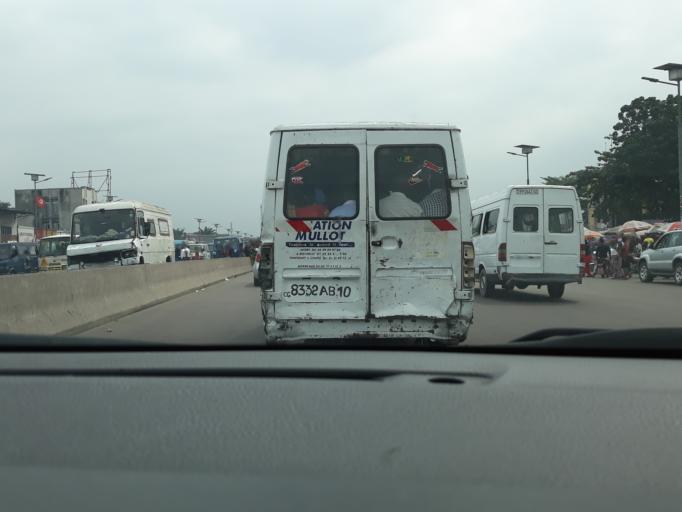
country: CD
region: Kinshasa
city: Masina
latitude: -4.4046
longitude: 15.4118
